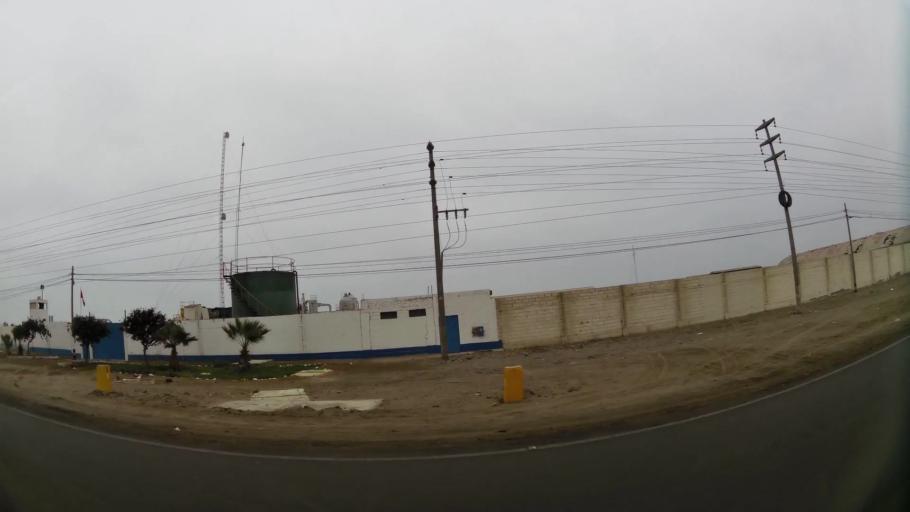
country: PE
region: Ica
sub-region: Provincia de Pisco
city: Paracas
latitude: -13.7955
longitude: -76.2400
